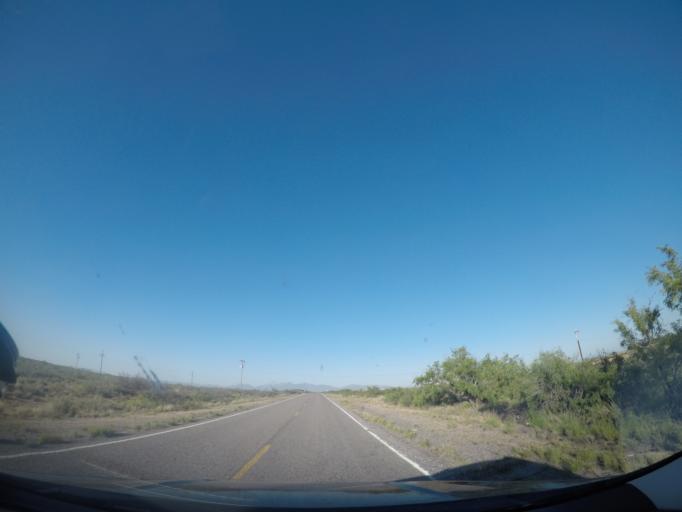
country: US
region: New Mexico
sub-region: Dona Ana County
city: Mesilla
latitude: 32.2661
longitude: -106.9783
